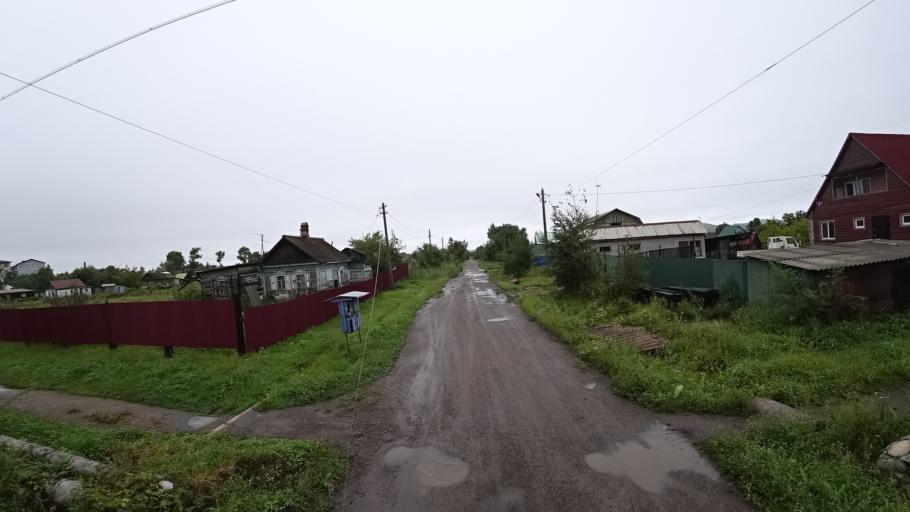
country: RU
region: Primorskiy
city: Monastyrishche
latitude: 44.2064
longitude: 132.4519
